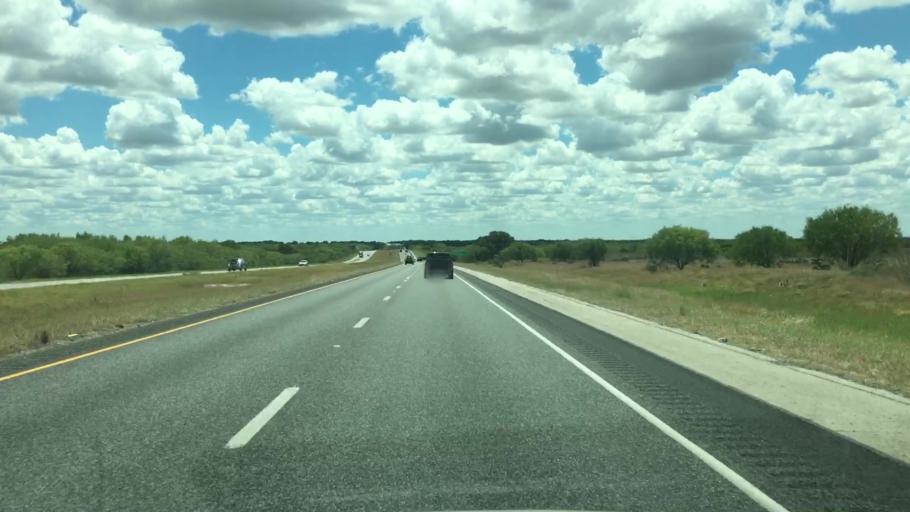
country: US
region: Texas
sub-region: Atascosa County
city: Pleasanton
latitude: 29.0949
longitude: -98.4330
